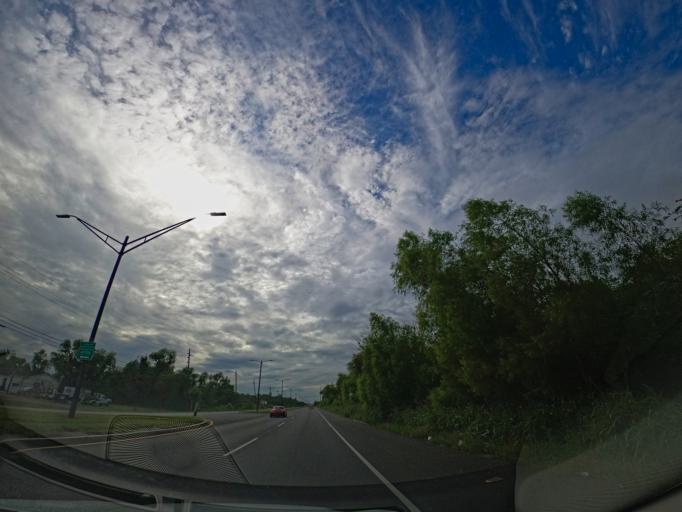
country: US
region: Louisiana
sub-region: Saint Bernard Parish
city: Chalmette
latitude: 30.0104
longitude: -89.9652
